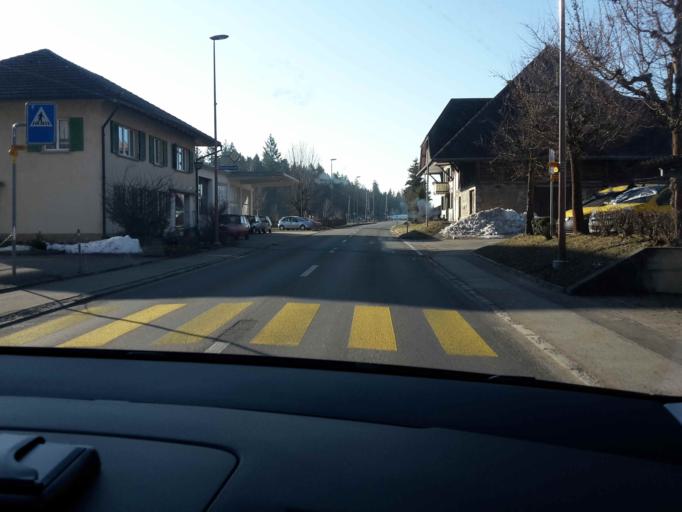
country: CH
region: Bern
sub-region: Emmental District
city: Sumiswald
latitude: 47.0610
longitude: 7.7496
